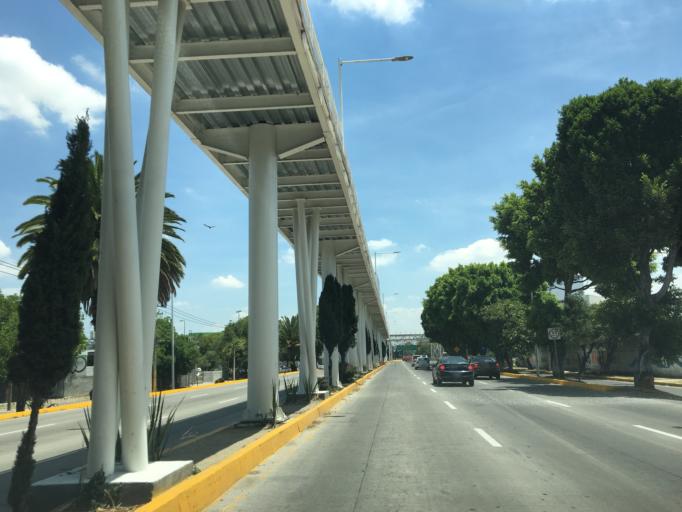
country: MX
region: Puebla
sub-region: Cuautlancingo
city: Sanctorum
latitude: 19.0889
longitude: -98.2293
